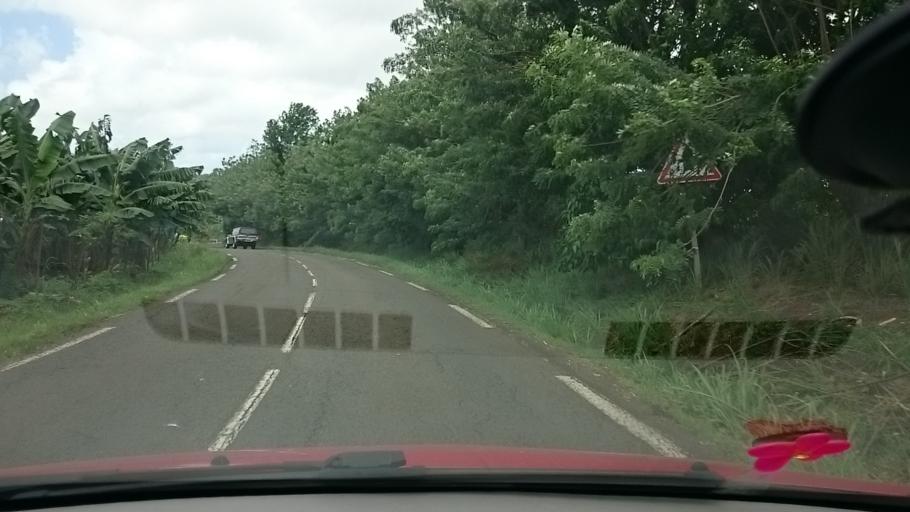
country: MQ
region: Martinique
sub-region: Martinique
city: Saint-Esprit
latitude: 14.5828
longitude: -60.9249
